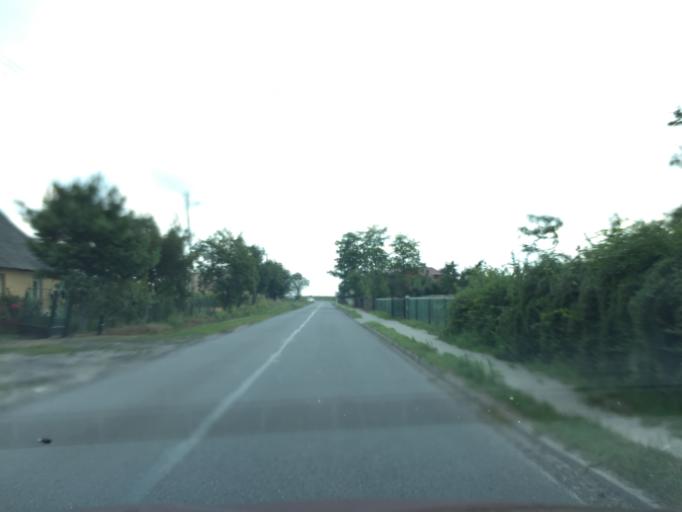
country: PL
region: Greater Poland Voivodeship
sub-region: Powiat kaliski
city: Stawiszyn
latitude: 51.9429
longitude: 18.1902
